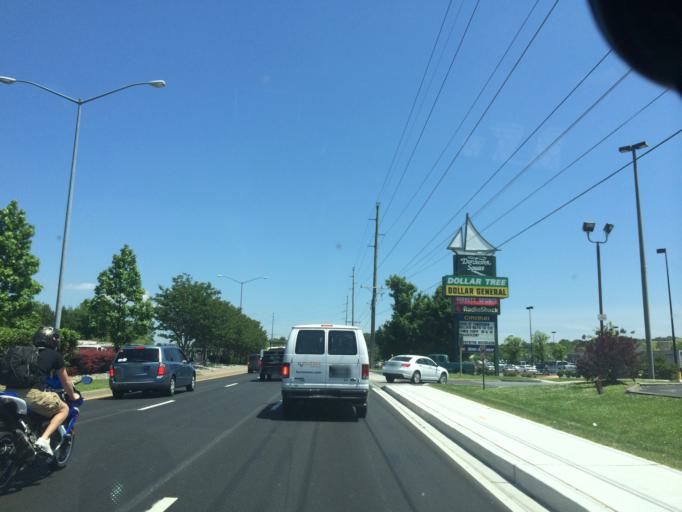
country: US
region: Maryland
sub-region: Dorchester County
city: Cambridge
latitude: 38.5552
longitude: -76.0538
